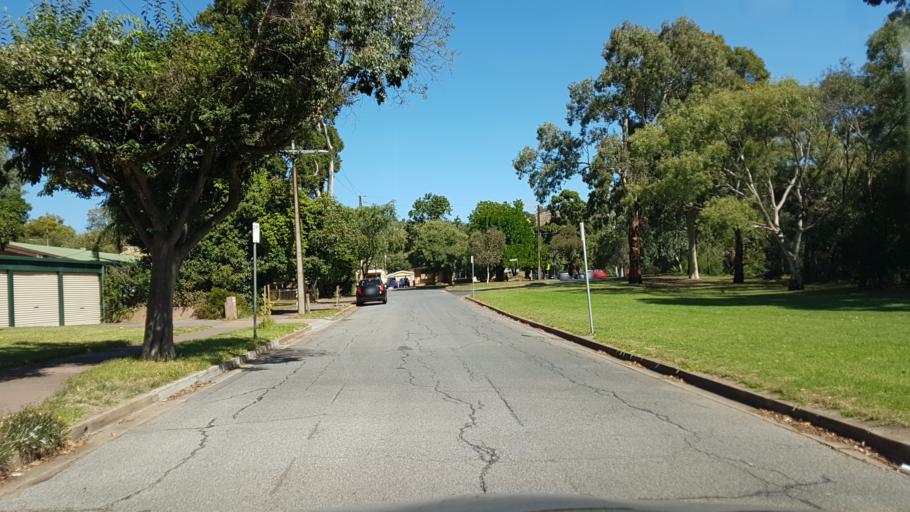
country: AU
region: South Australia
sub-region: Onkaparinga
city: Bedford Park
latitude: -35.0254
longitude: 138.5642
